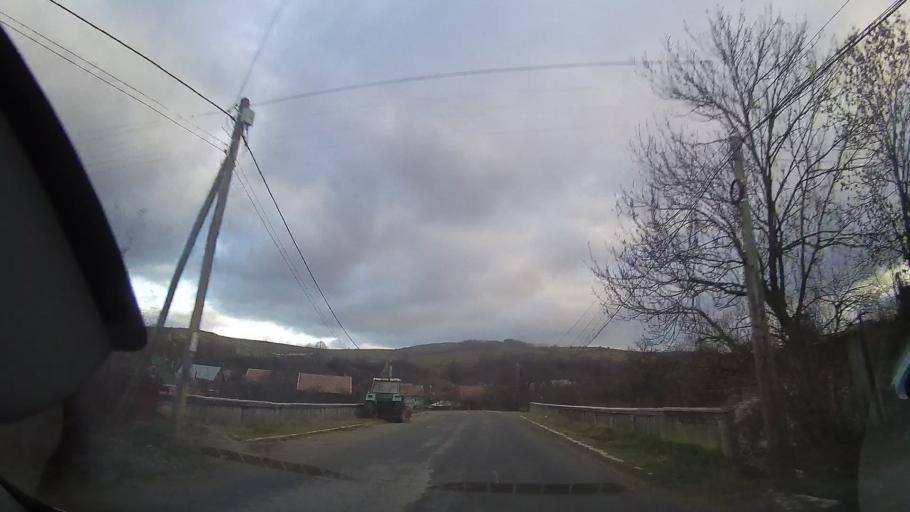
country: RO
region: Cluj
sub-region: Comuna Sancraiu
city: Sancraiu
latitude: 46.8032
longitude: 22.9965
